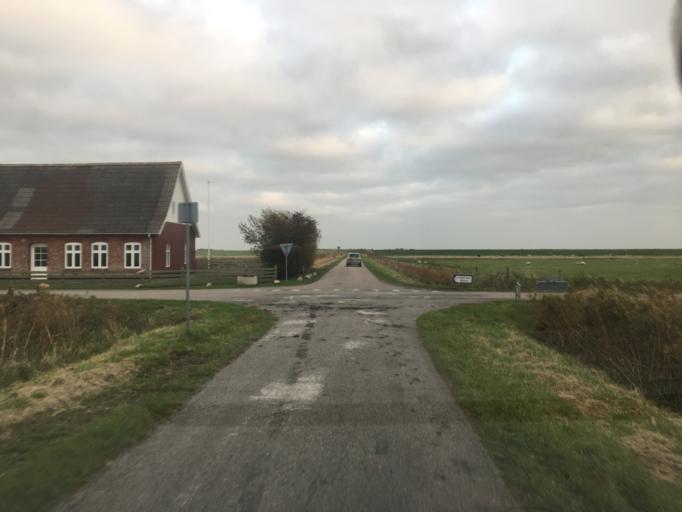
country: DE
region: Schleswig-Holstein
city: Klanxbull
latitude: 54.9262
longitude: 8.6785
